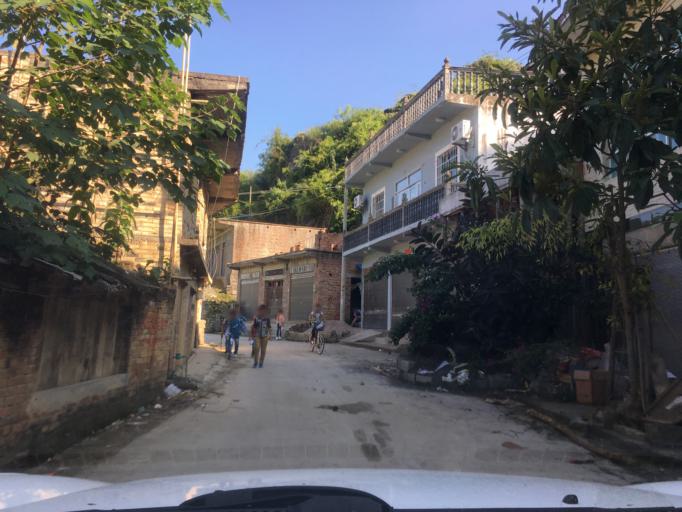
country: CN
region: Guangxi Zhuangzu Zizhiqu
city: Xinzhou
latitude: 25.4427
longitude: 105.7371
